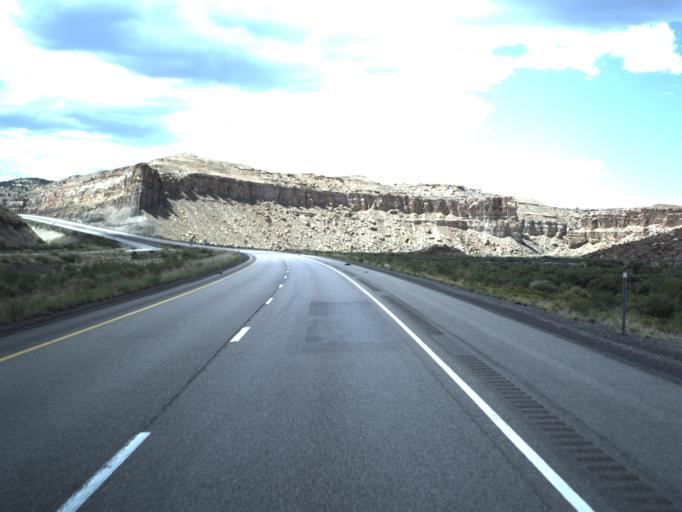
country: US
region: Utah
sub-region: Emery County
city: Ferron
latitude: 38.8102
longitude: -111.2497
